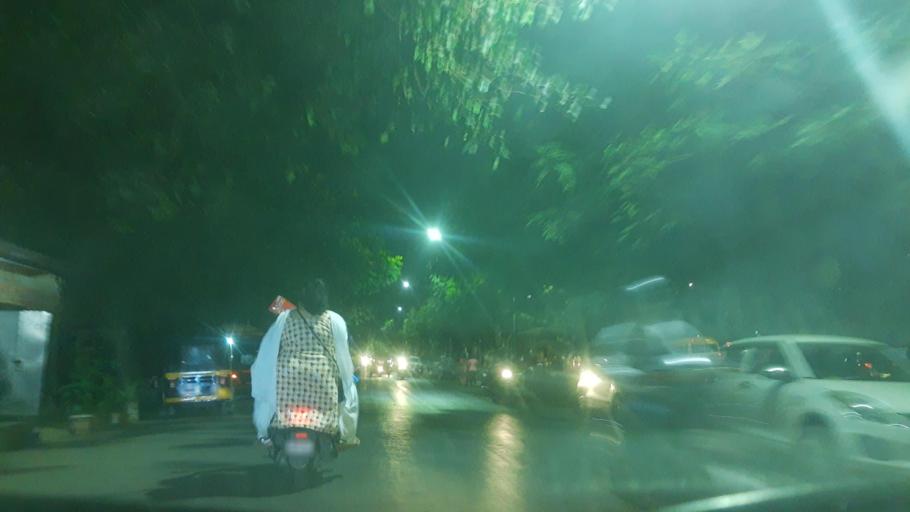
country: IN
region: Maharashtra
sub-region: Thane
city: Thane
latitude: 19.2099
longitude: 72.9749
